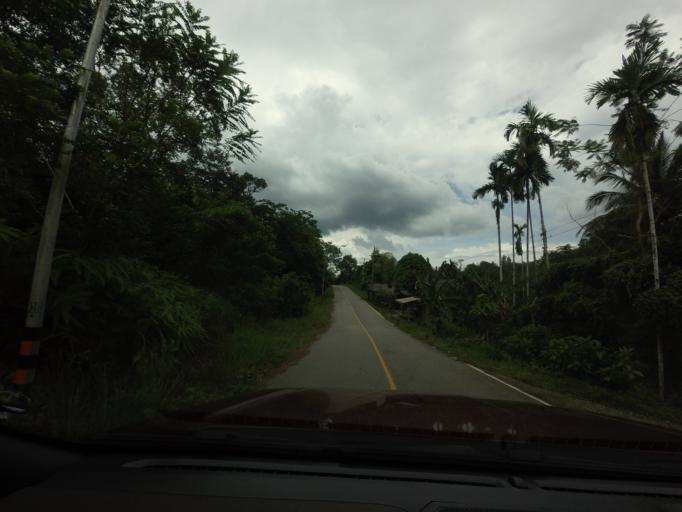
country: TH
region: Narathiwat
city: Sukhirin
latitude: 5.9928
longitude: 101.7028
